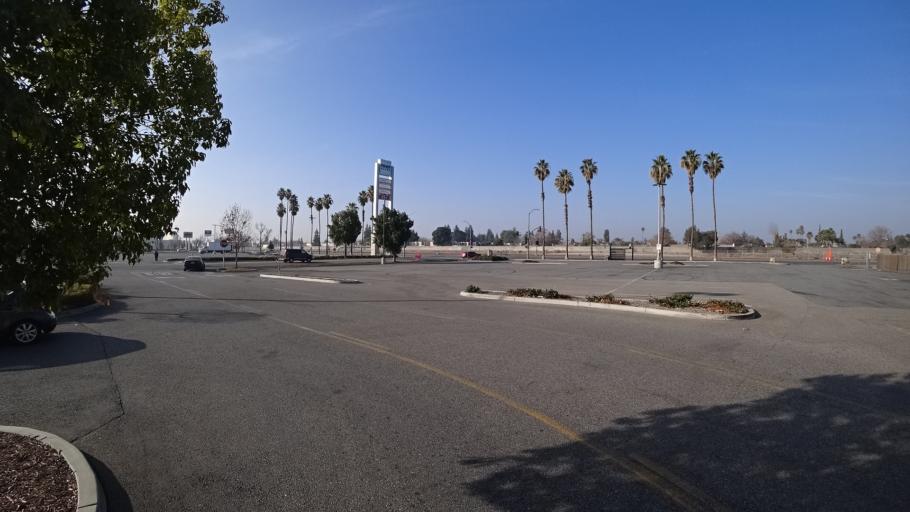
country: US
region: California
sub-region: Kern County
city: Bakersfield
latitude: 35.3369
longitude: -119.0381
